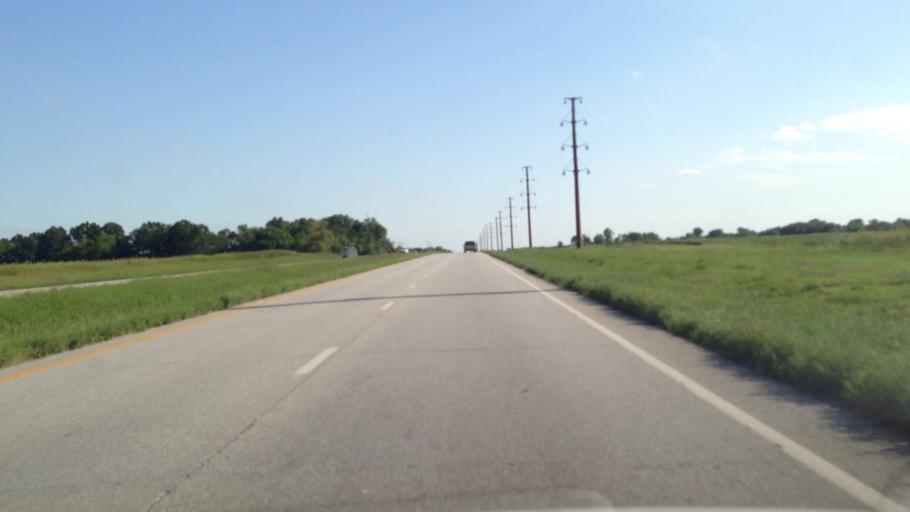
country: US
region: Kansas
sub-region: Crawford County
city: Frontenac
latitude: 37.4961
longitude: -94.7053
